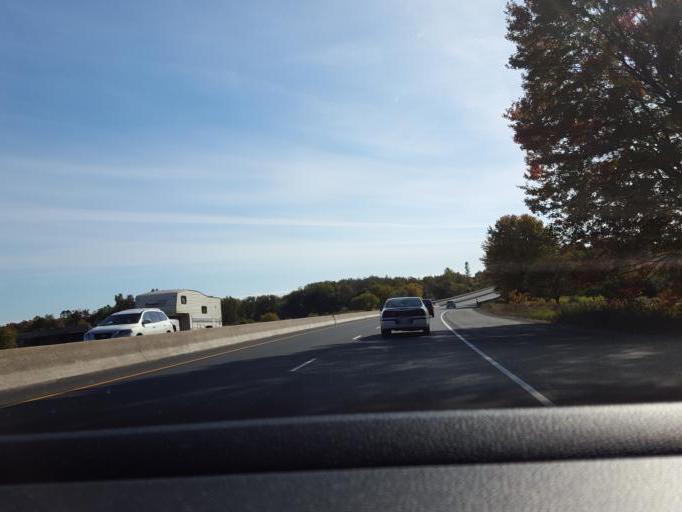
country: CA
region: Ontario
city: Oshawa
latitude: 43.9293
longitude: -78.5993
